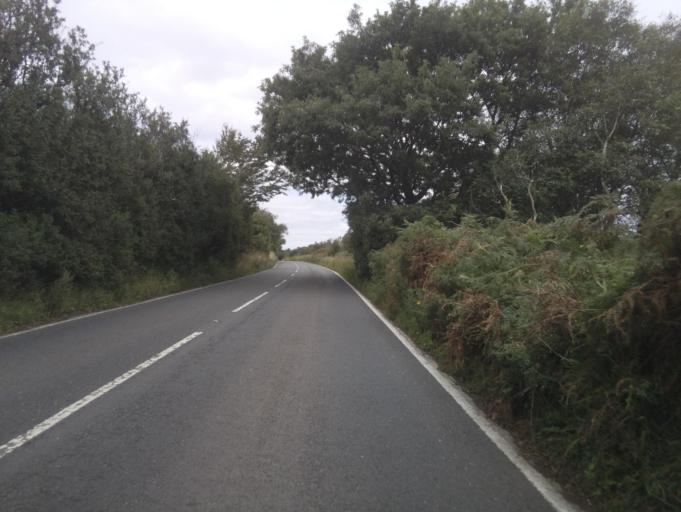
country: GB
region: England
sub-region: Devon
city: Bishopsteignton
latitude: 50.5743
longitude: -3.5270
